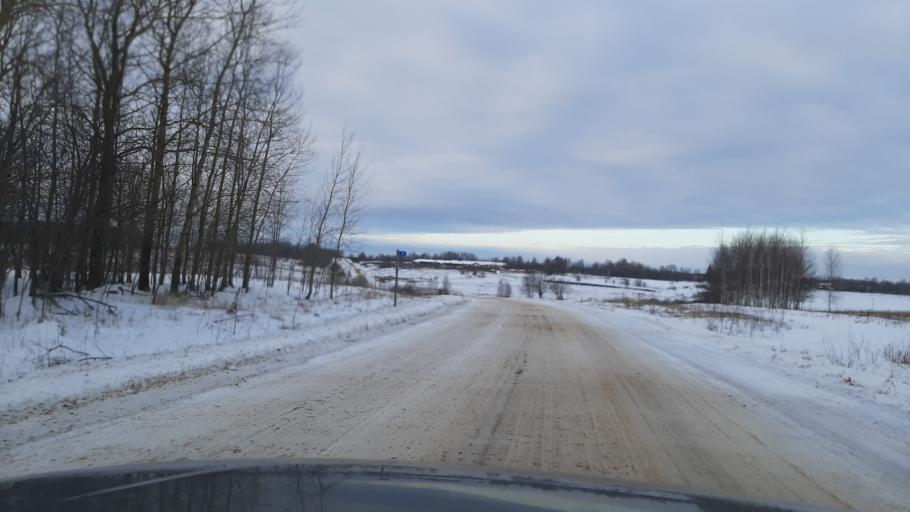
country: RU
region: Kostroma
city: Kosmynino
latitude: 57.4805
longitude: 40.7428
